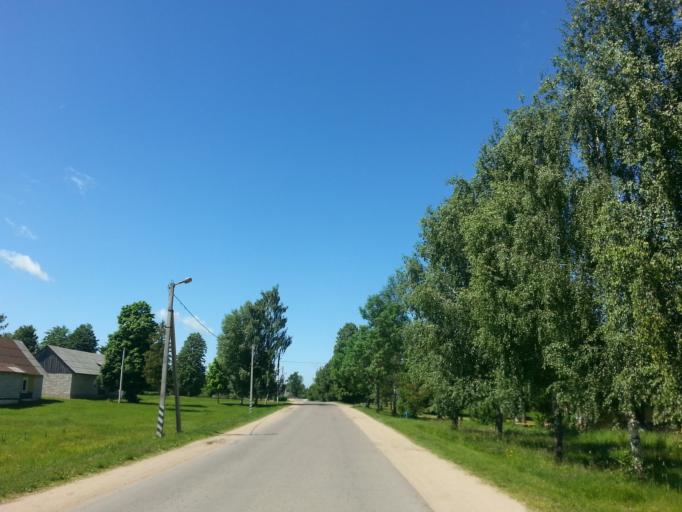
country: BY
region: Vitebsk
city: Mosar
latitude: 55.2106
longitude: 27.5648
